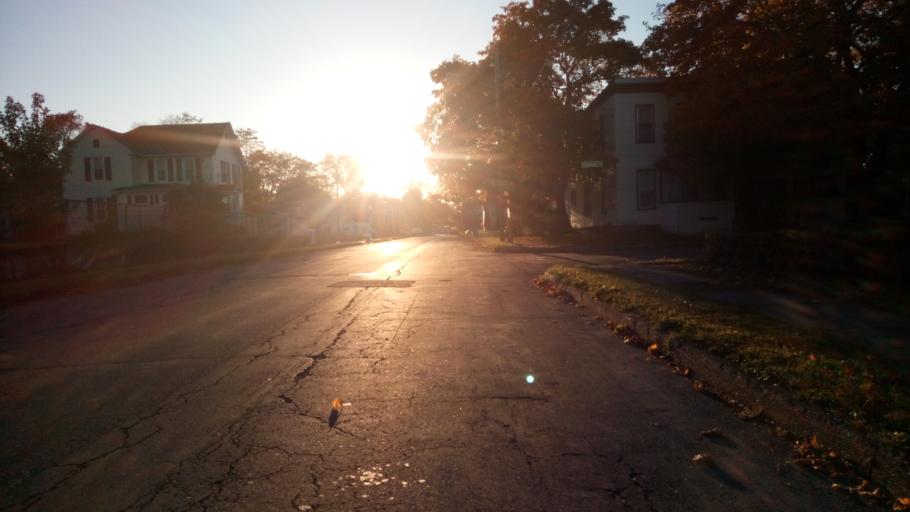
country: US
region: New York
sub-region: Chemung County
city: Elmira
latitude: 42.0810
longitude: -76.8093
